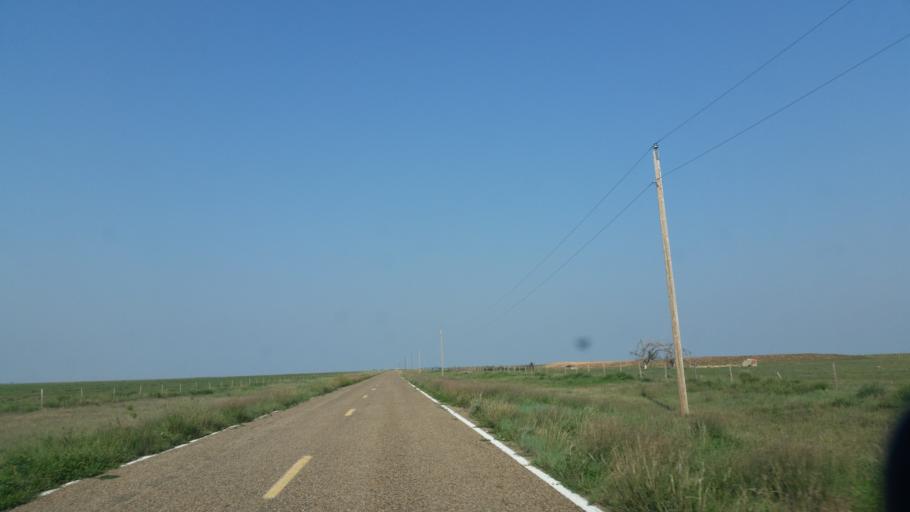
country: US
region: New Mexico
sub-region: Quay County
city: Logan
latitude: 34.9234
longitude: -103.3430
